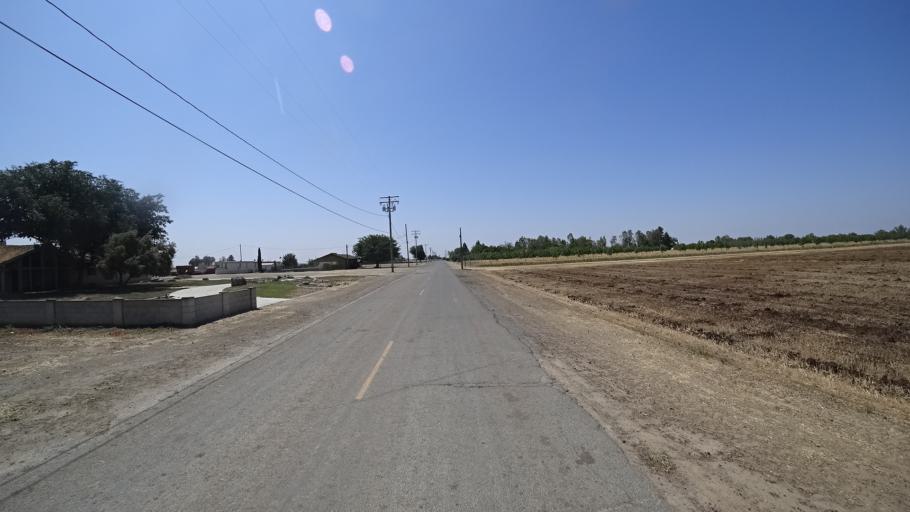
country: US
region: California
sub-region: Kings County
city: Home Garden
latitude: 36.3047
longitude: -119.6100
